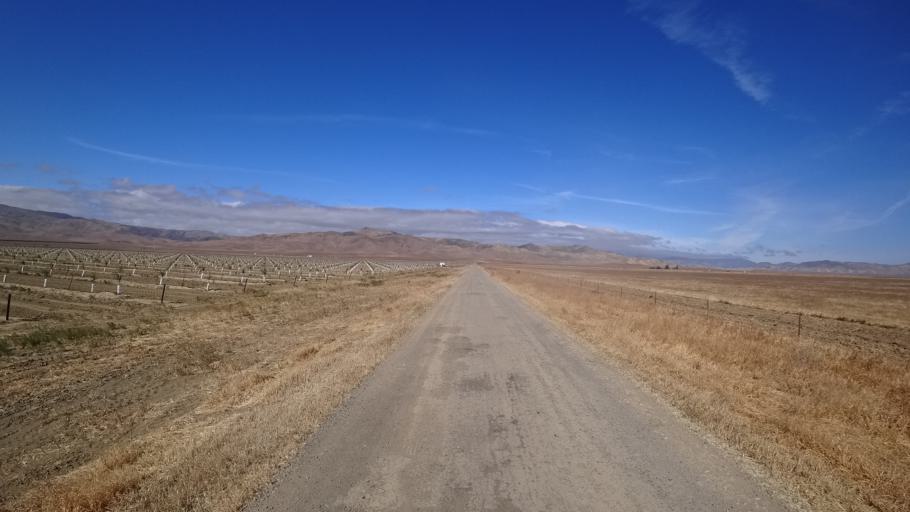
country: US
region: California
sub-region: Kings County
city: Avenal
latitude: 35.8178
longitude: -120.0865
